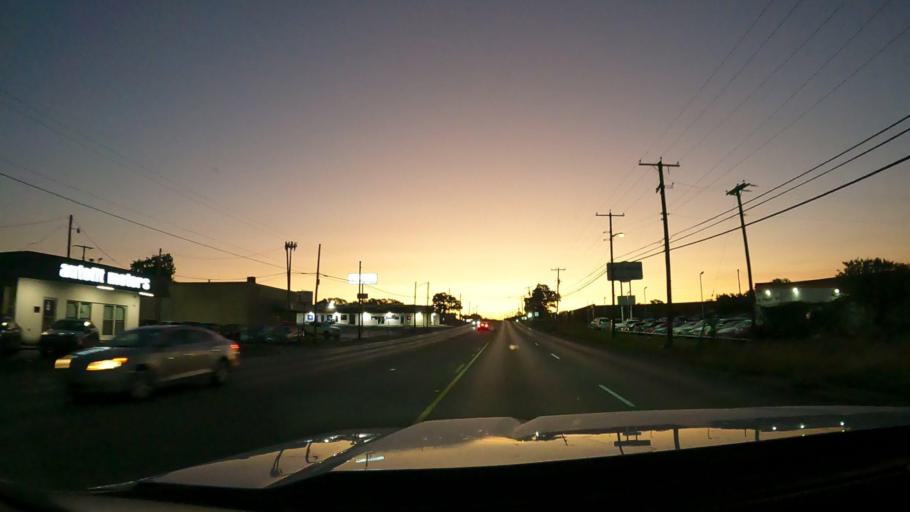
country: US
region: Texas
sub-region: Tarrant County
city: Pantego
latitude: 32.7358
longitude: -97.1392
